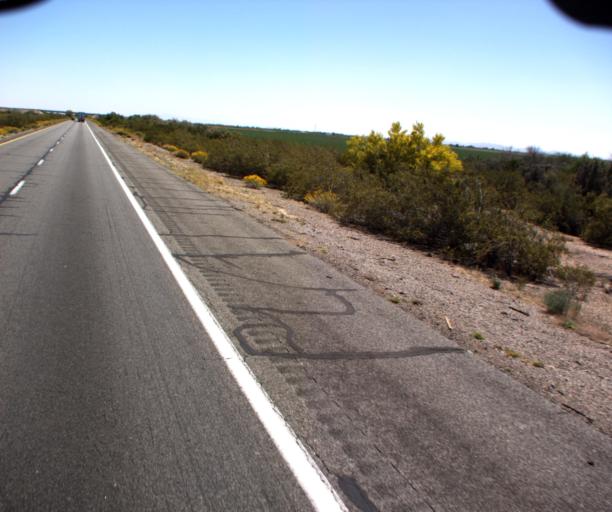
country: US
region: Arizona
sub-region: Maricopa County
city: Buckeye
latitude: 33.4916
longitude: -112.9120
